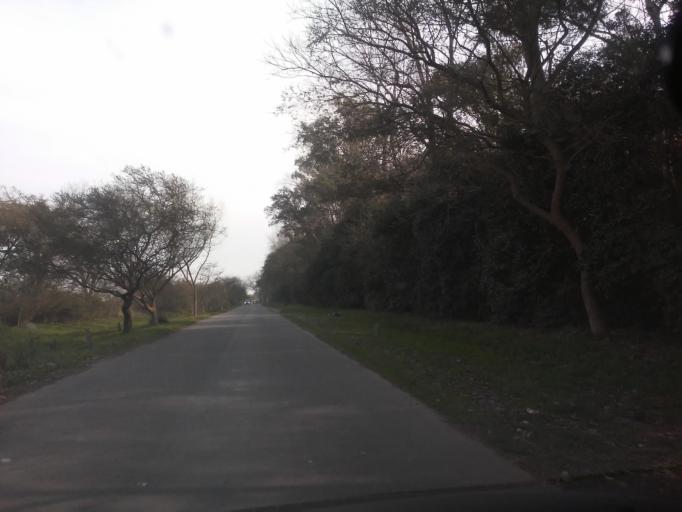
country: AR
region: Buenos Aires
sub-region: Partido de Marcos Paz
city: Marcos Paz
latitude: -34.6714
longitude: -58.8574
